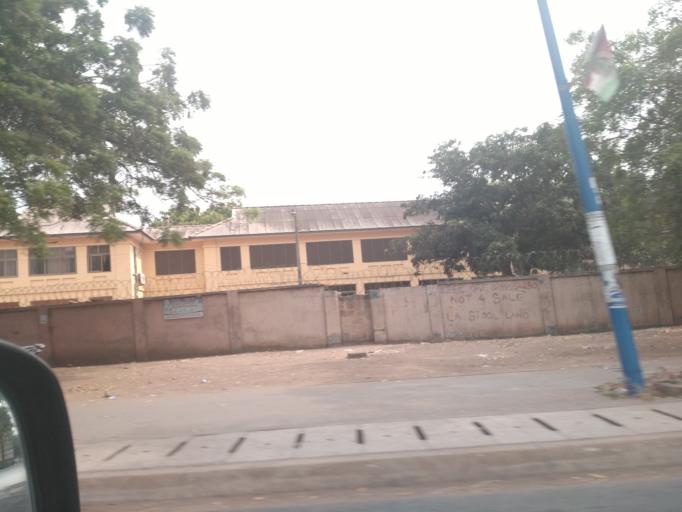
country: GH
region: Greater Accra
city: Accra
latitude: 5.5904
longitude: -0.1828
